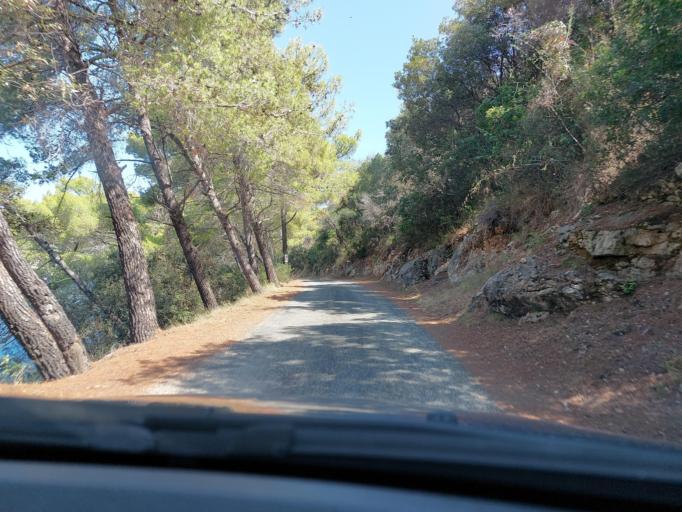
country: HR
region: Dubrovacko-Neretvanska
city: Smokvica
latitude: 42.7704
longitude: 16.8370
